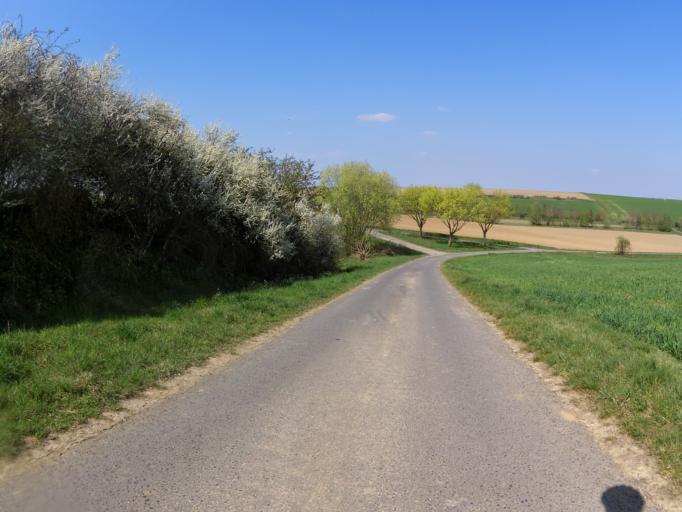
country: DE
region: Bavaria
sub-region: Regierungsbezirk Unterfranken
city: Dettelbach
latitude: 49.8184
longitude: 10.1345
